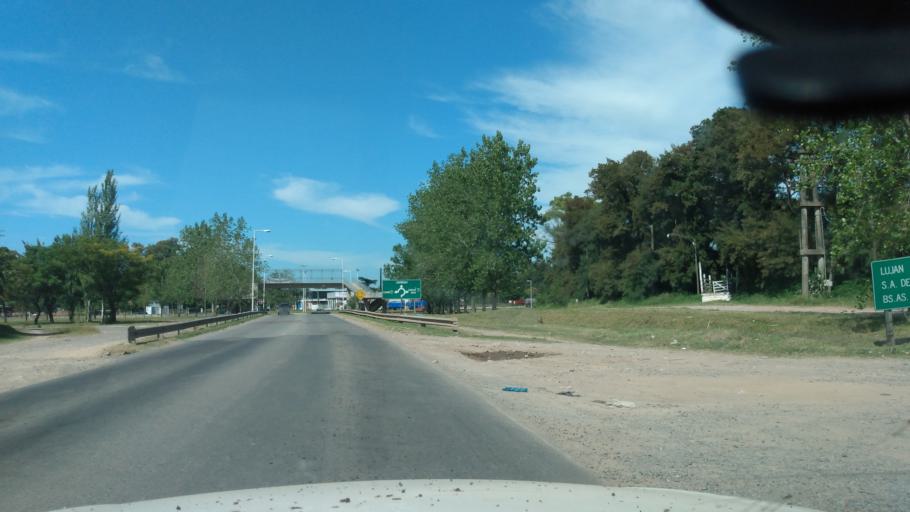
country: AR
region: Buenos Aires
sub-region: Partido de Lujan
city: Lujan
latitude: -34.5489
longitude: -59.1247
